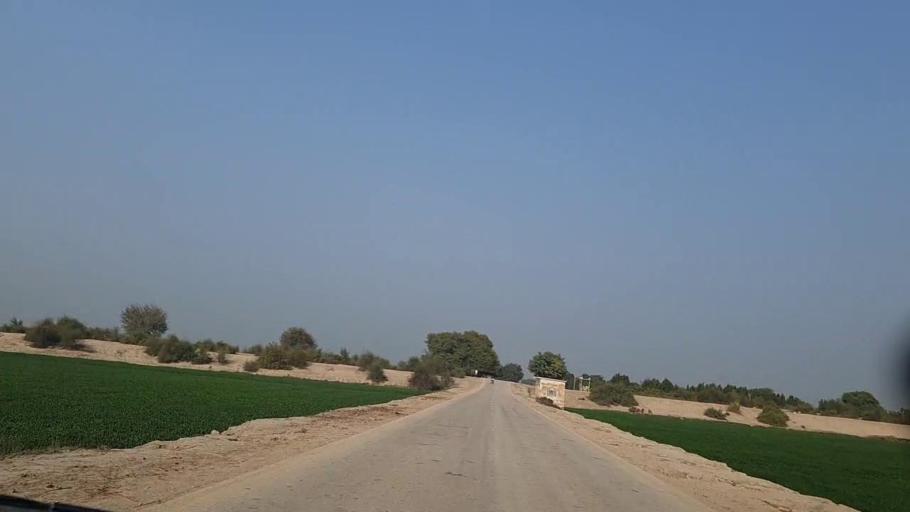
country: PK
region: Sindh
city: Sann
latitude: 26.1765
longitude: 68.1074
